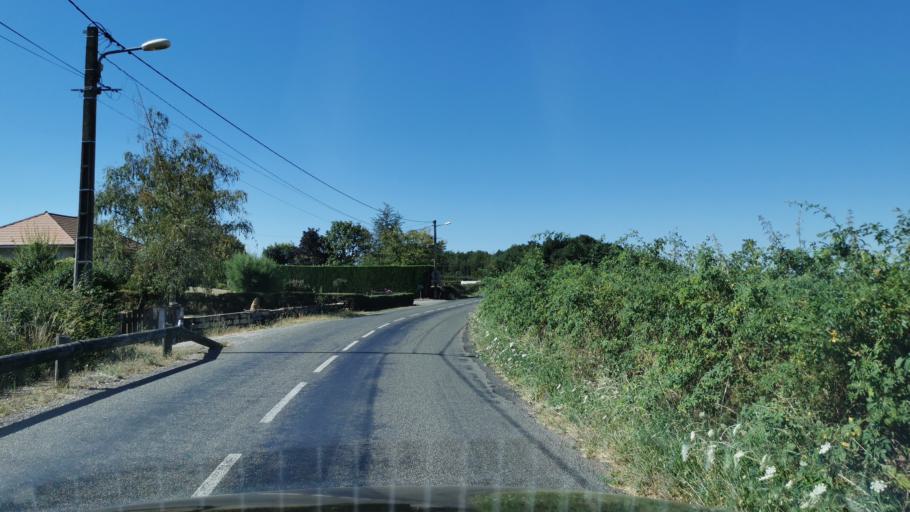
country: FR
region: Bourgogne
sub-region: Departement de Saone-et-Loire
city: Torcy
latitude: 46.7785
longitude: 4.4757
